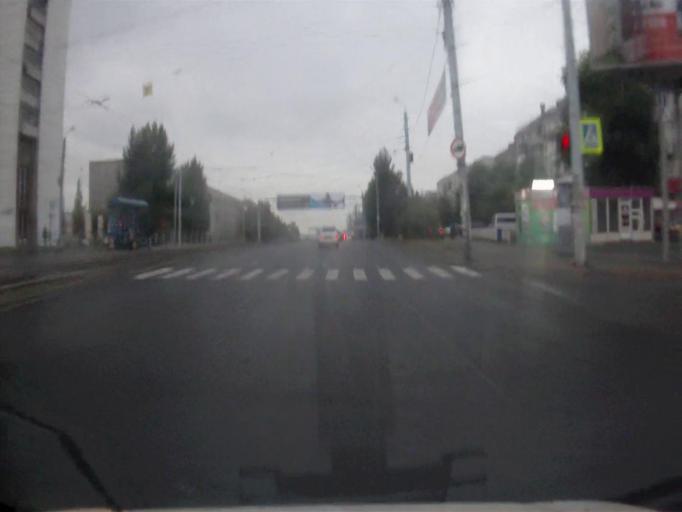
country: RU
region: Chelyabinsk
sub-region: Gorod Chelyabinsk
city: Chelyabinsk
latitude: 55.1840
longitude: 61.3869
